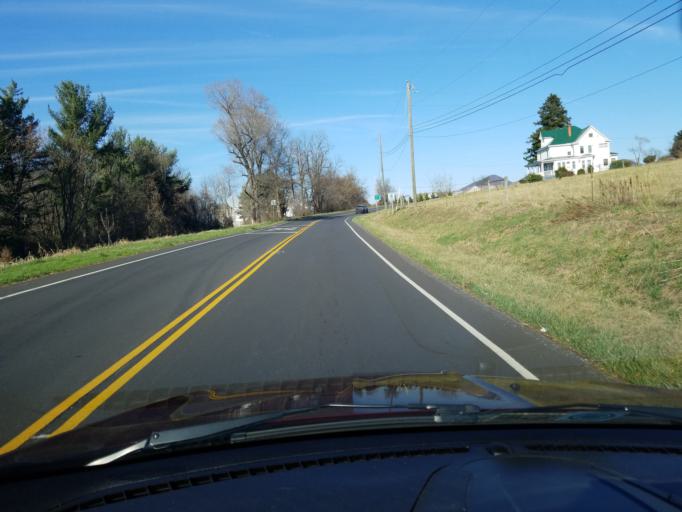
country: US
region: Virginia
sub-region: Botetourt County
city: Cloverdale
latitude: 37.3508
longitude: -79.9208
